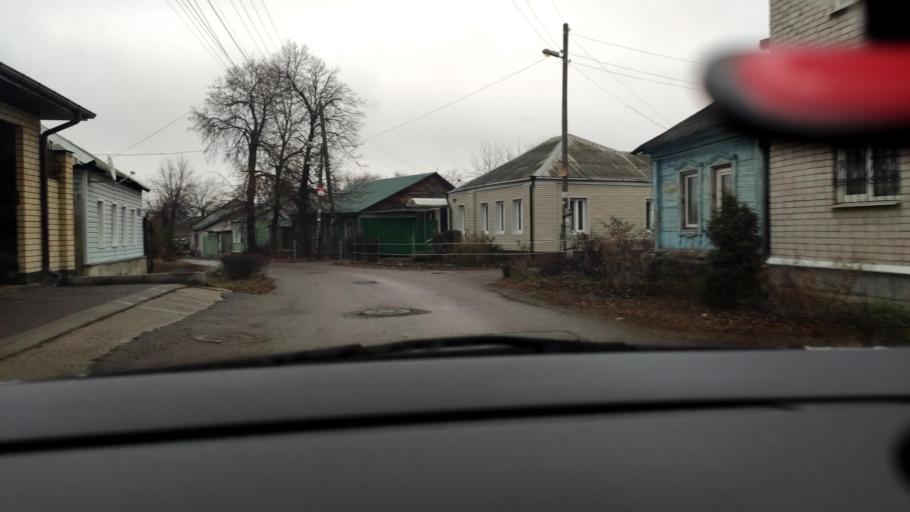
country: RU
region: Voronezj
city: Voronezh
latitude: 51.6483
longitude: 39.2005
